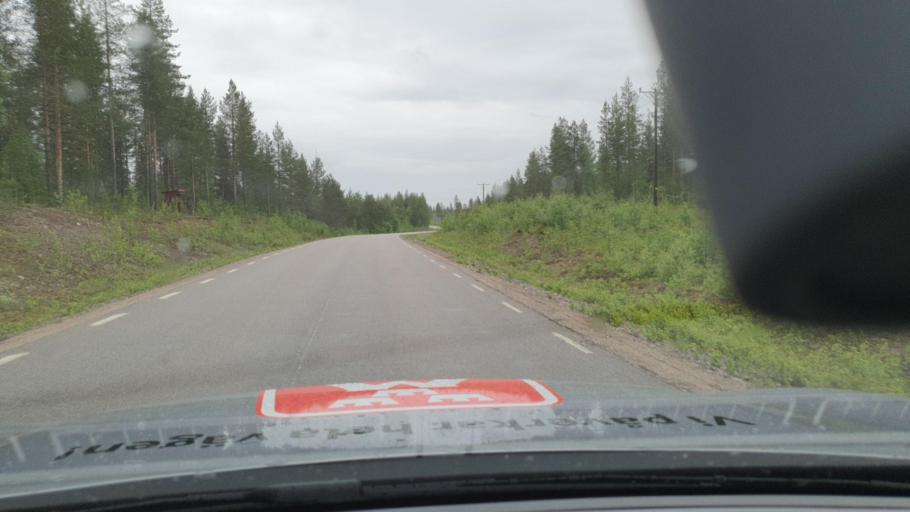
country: SE
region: Norrbotten
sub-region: Pajala Kommun
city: Pajala
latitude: 66.7645
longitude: 23.1538
